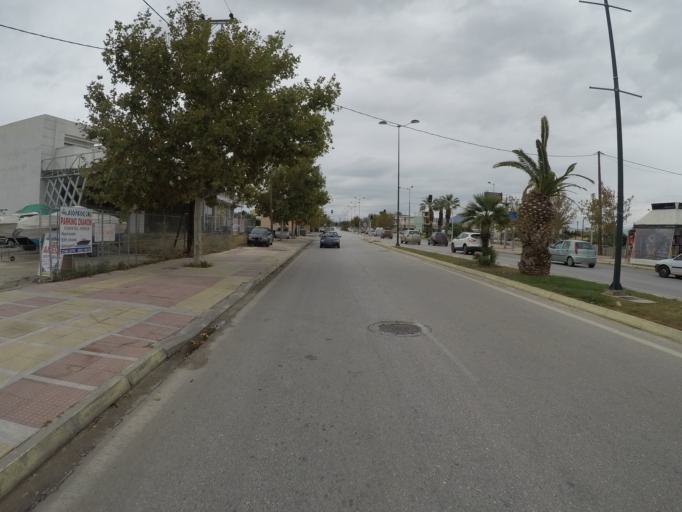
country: GR
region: Peloponnese
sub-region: Nomos Korinthias
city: Loutraki
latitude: 37.9584
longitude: 22.9793
